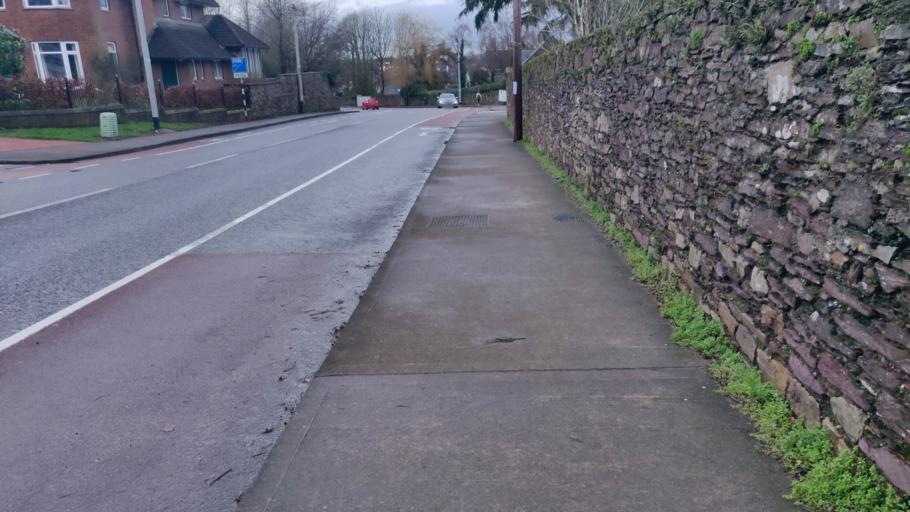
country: IE
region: Munster
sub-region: County Cork
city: Cork
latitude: 51.8754
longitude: -8.4280
